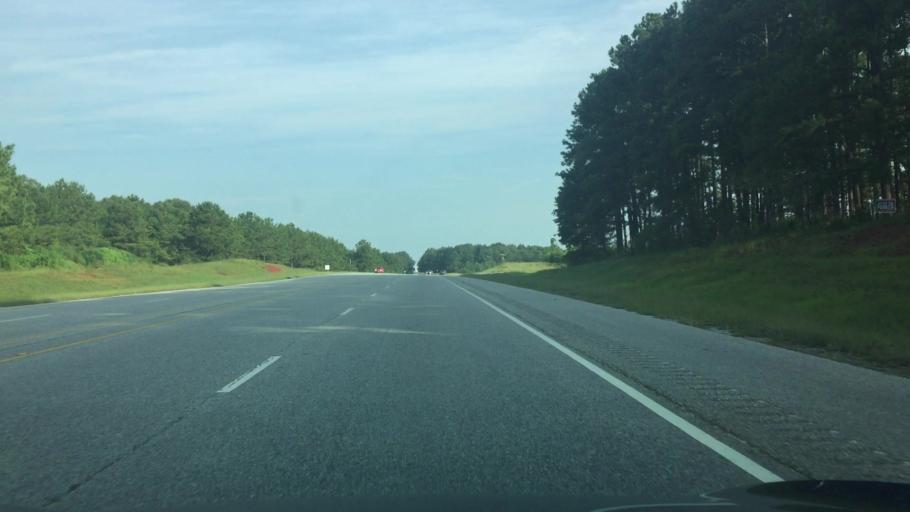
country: US
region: Alabama
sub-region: Butler County
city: Georgiana
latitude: 31.5021
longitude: -86.6978
